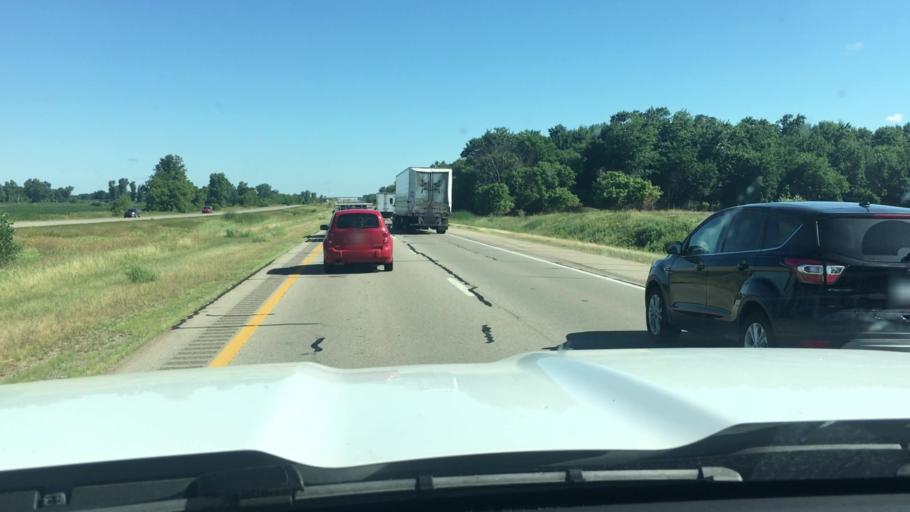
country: US
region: Michigan
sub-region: Clinton County
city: Saint Johns
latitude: 42.9625
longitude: -84.5185
